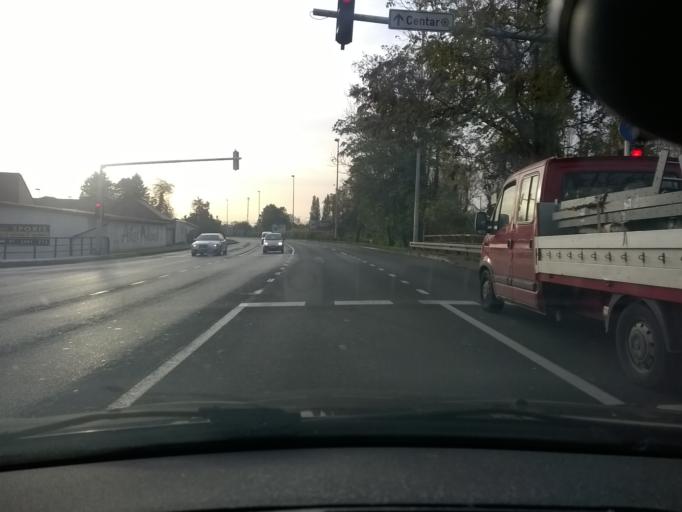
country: HR
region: Zagrebacka
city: Bestovje
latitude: 45.8178
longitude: 15.8310
